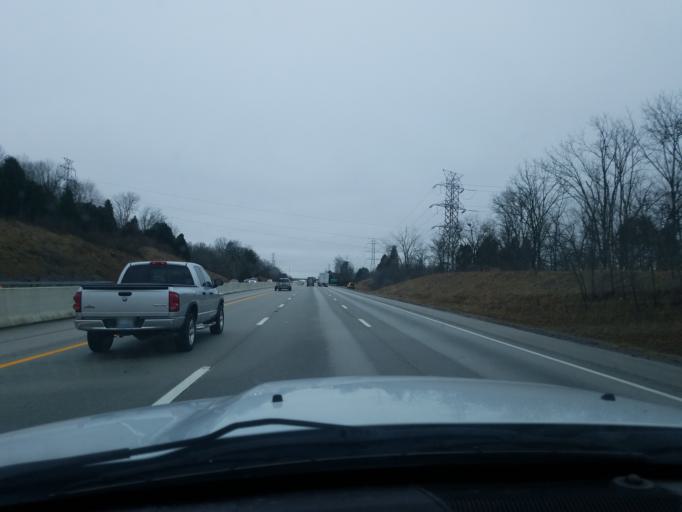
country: US
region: Kentucky
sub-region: Jefferson County
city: Middletown
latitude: 38.2222
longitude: -85.4826
